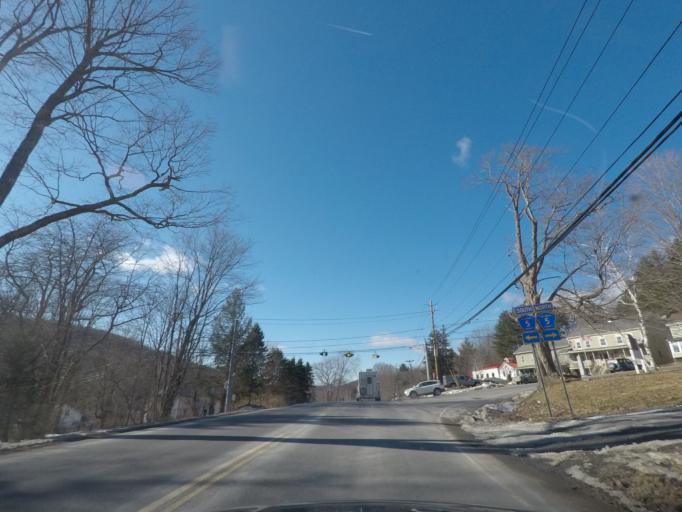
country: US
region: Massachusetts
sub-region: Berkshire County
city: Richmond
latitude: 42.4123
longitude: -73.4473
